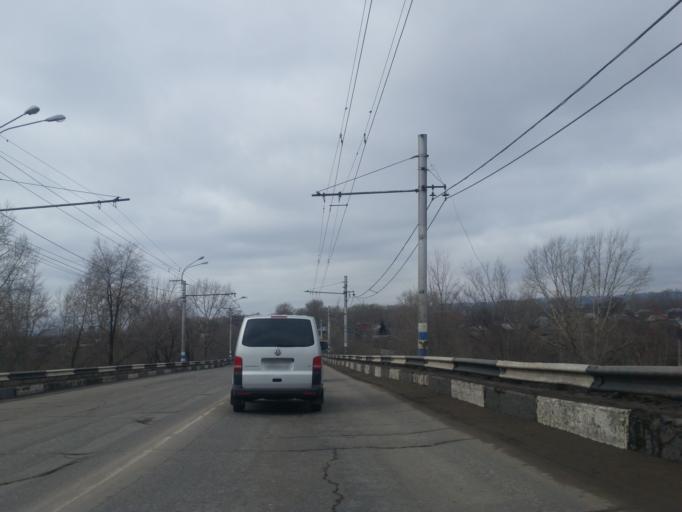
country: RU
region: Ulyanovsk
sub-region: Ulyanovskiy Rayon
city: Ulyanovsk
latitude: 54.3321
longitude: 48.5063
